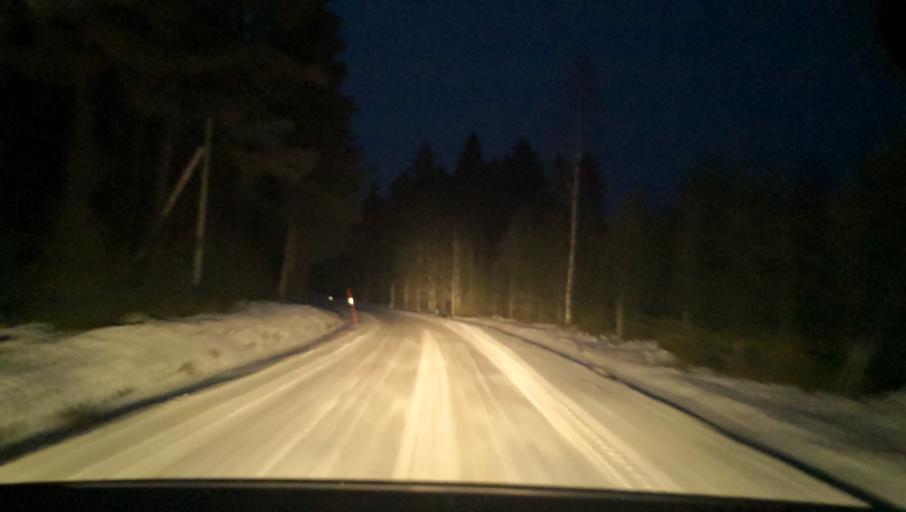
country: SE
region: Uppsala
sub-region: Heby Kommun
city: Tarnsjo
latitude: 60.2797
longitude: 16.8033
